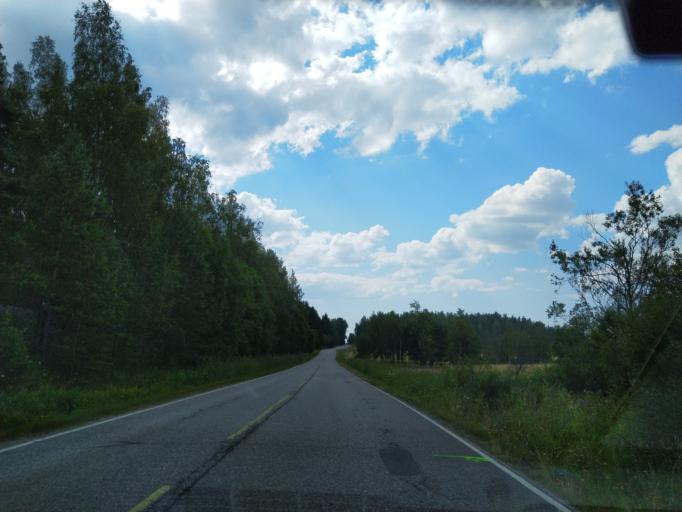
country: FI
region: Uusimaa
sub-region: Helsinki
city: Kirkkonummi
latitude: 60.0888
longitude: 24.5025
